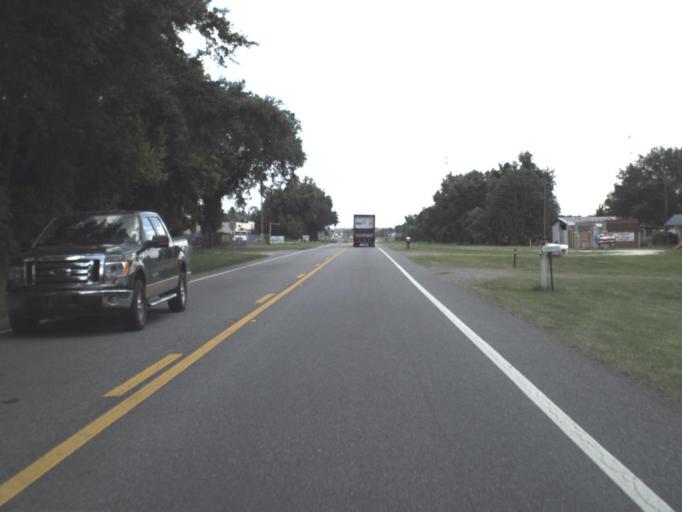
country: US
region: Florida
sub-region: Alachua County
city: High Springs
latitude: 30.0089
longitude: -82.5974
